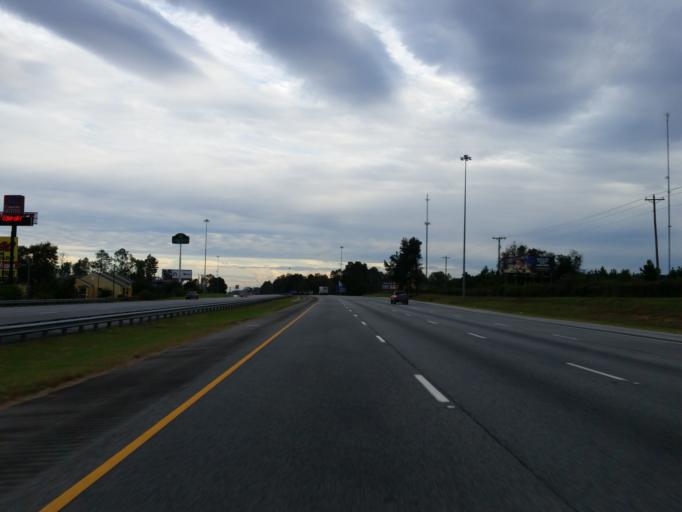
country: US
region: Georgia
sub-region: Lowndes County
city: Remerton
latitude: 30.8423
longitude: -83.3299
